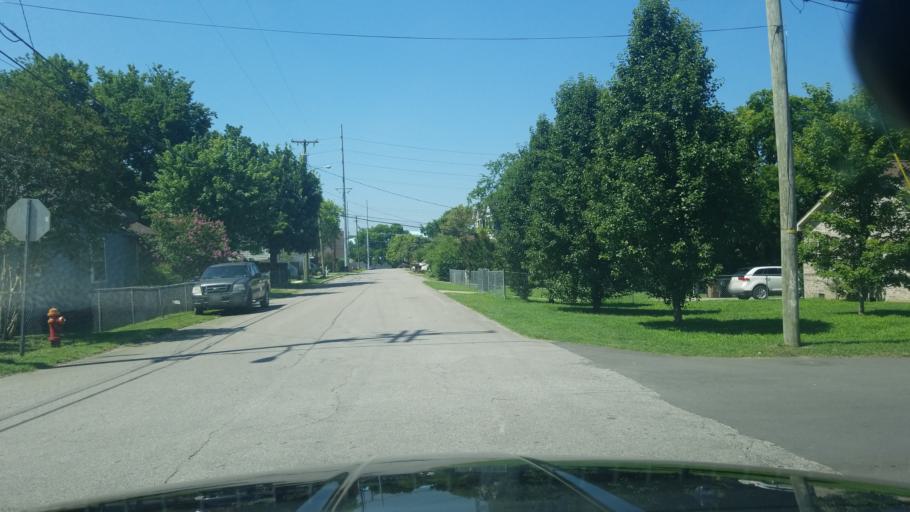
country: US
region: Tennessee
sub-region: Davidson County
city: Belle Meade
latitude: 36.1650
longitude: -86.8613
